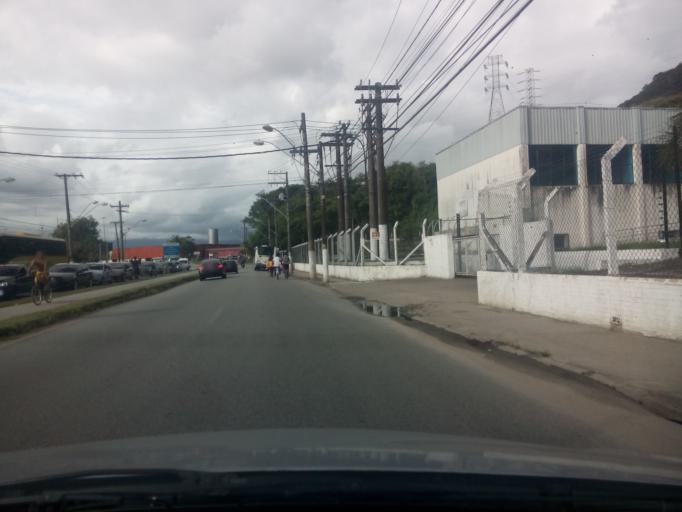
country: BR
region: Sao Paulo
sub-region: Guaruja
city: Guaruja
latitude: -23.9863
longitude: -46.2650
